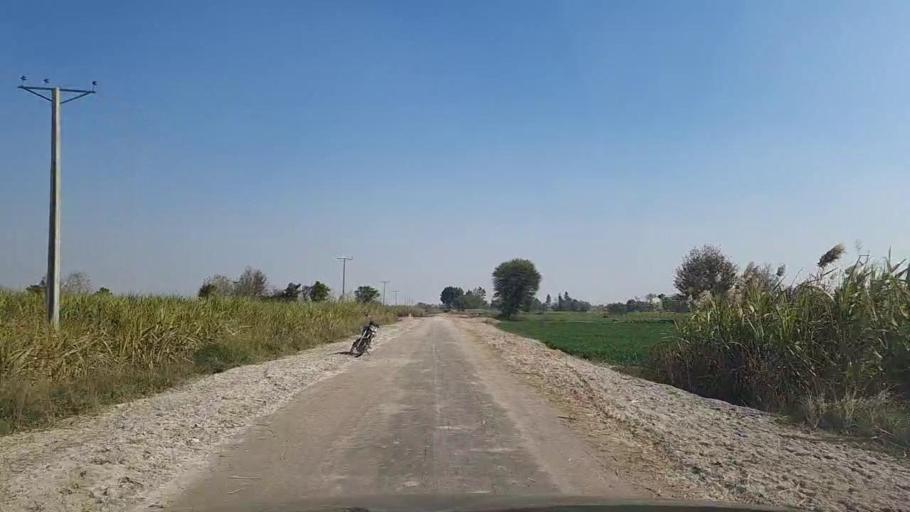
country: PK
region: Sindh
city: Bandhi
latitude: 26.5556
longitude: 68.3597
